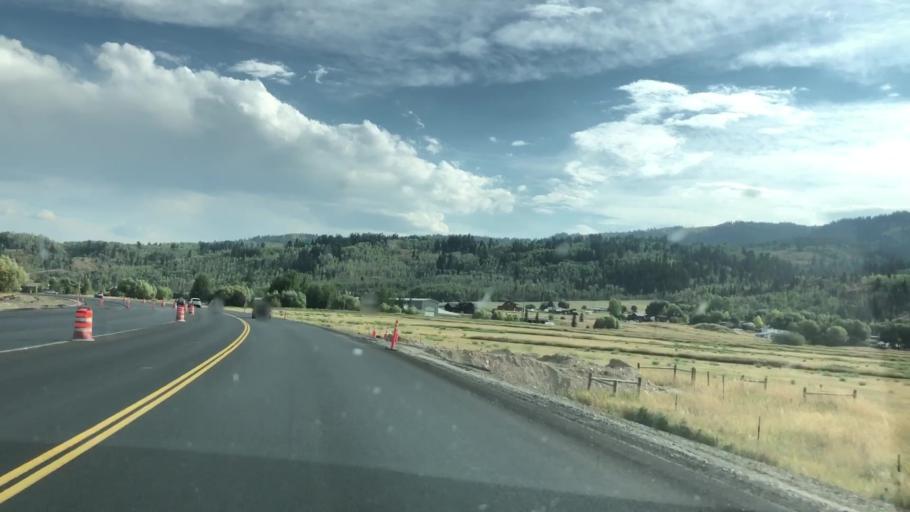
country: US
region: Wyoming
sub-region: Teton County
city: South Park
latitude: 43.3762
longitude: -110.7450
